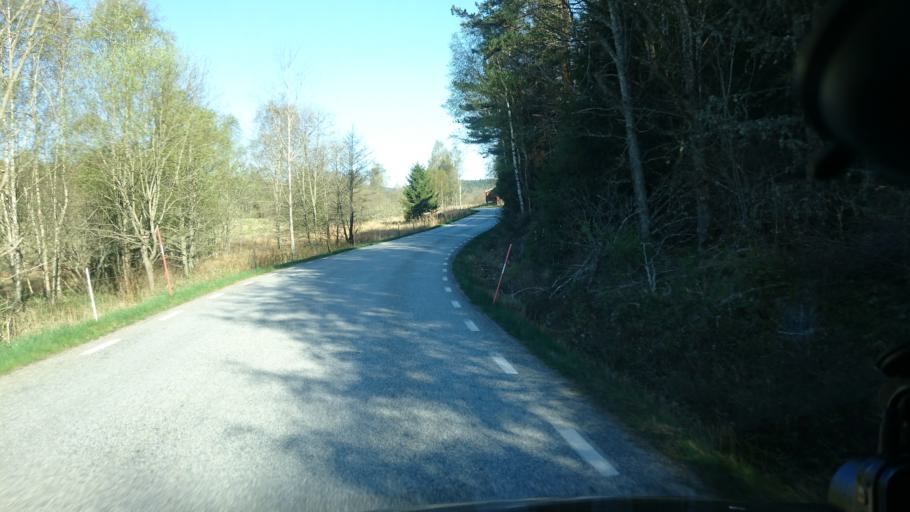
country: SE
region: Vaestra Goetaland
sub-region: Munkedals Kommun
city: Munkedal
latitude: 58.3716
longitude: 11.6891
